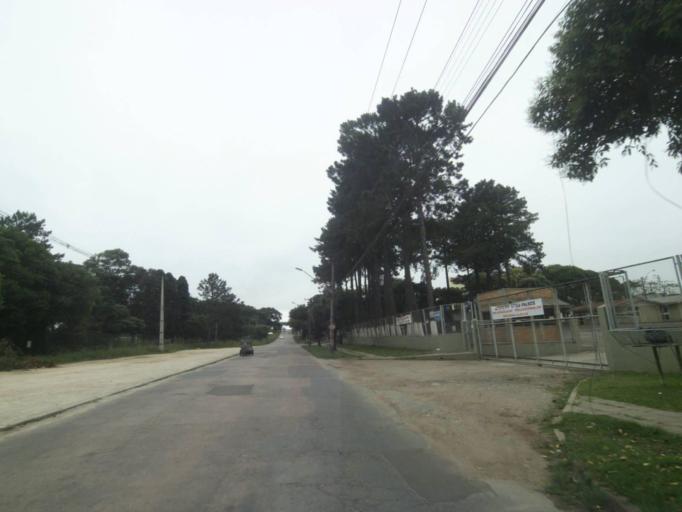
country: BR
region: Parana
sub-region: Araucaria
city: Araucaria
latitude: -25.5379
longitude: -49.3191
